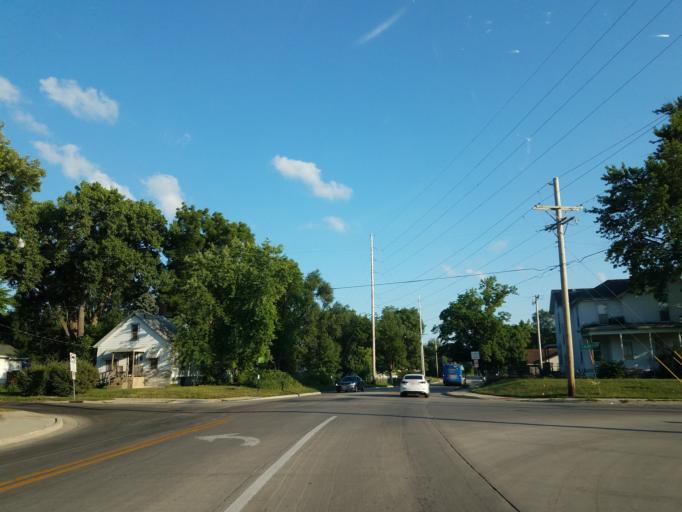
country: US
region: Illinois
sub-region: McLean County
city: Bloomington
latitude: 40.4764
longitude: -89.0162
